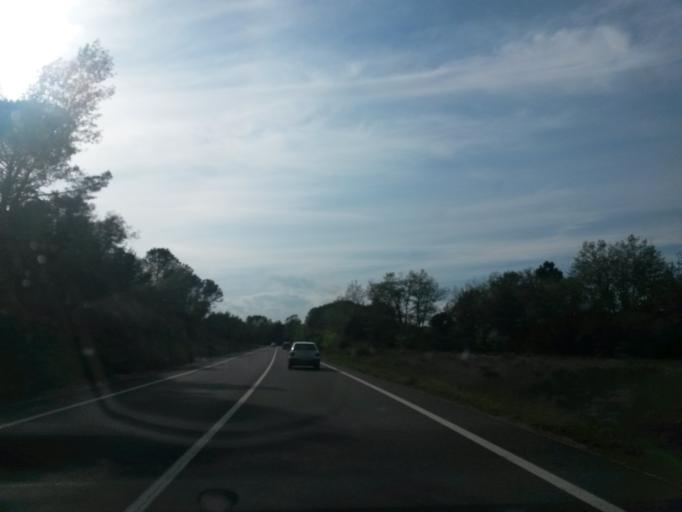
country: ES
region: Catalonia
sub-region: Provincia de Girona
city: Caldes de Malavella
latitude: 41.8433
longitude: 2.7865
